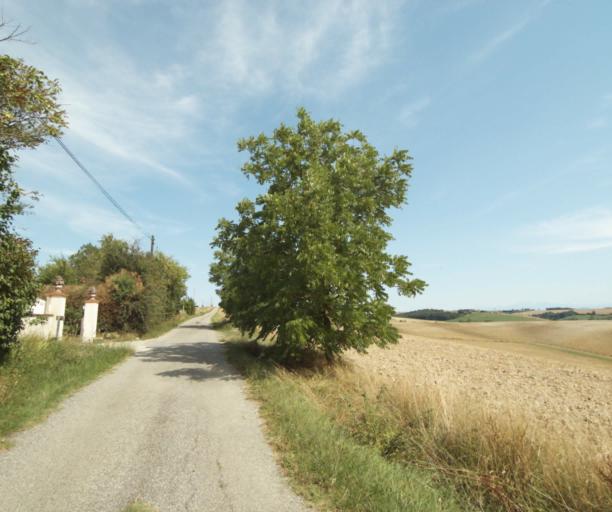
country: FR
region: Midi-Pyrenees
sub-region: Departement de l'Ariege
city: Lezat-sur-Leze
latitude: 43.2653
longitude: 1.4004
